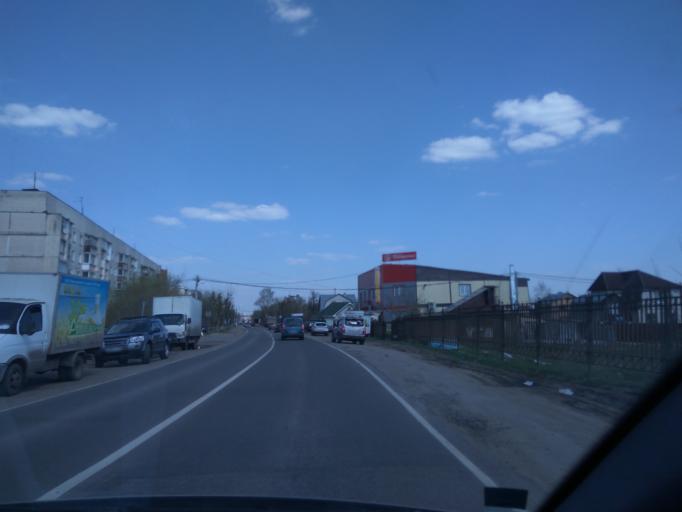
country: RU
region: Moskovskaya
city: Ramenskoye
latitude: 55.5478
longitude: 38.2506
